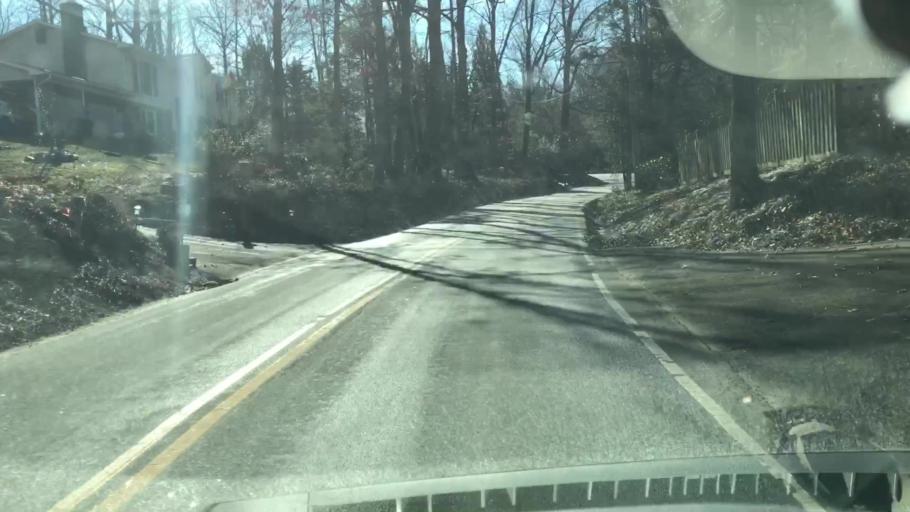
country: US
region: Virginia
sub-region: Fairfax County
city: Oakton
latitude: 38.8693
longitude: -77.3364
